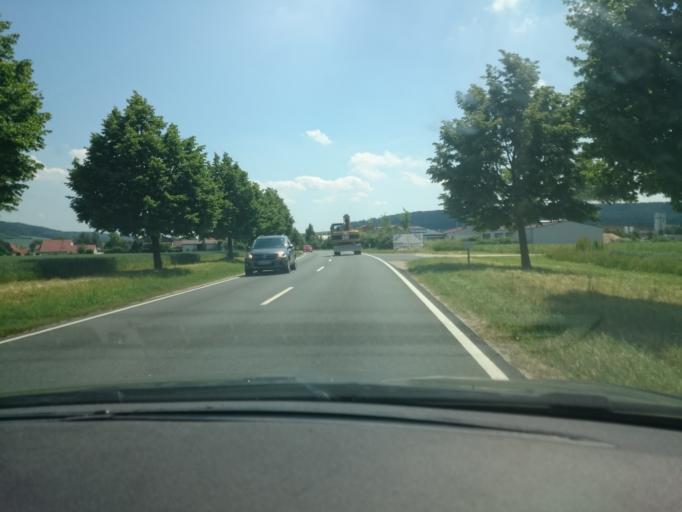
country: DE
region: Bavaria
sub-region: Regierungsbezirk Mittelfranken
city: Thalmassing
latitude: 49.1493
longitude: 11.2591
